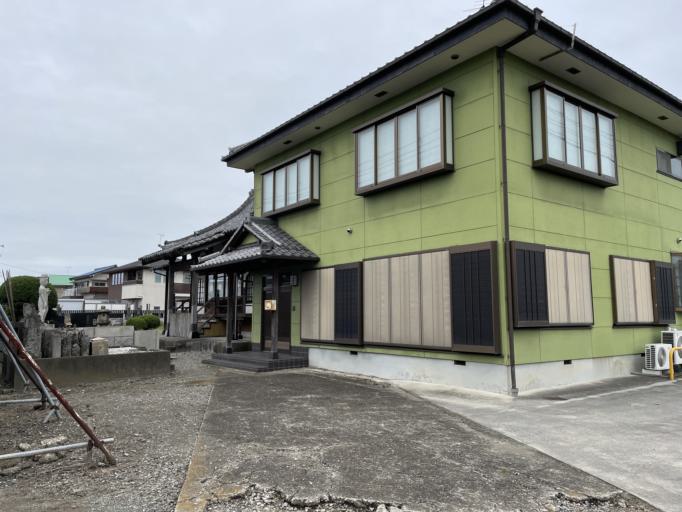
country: JP
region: Saitama
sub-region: Kawaguchi-shi
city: Hatogaya-honcho
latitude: 35.8067
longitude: 139.7647
